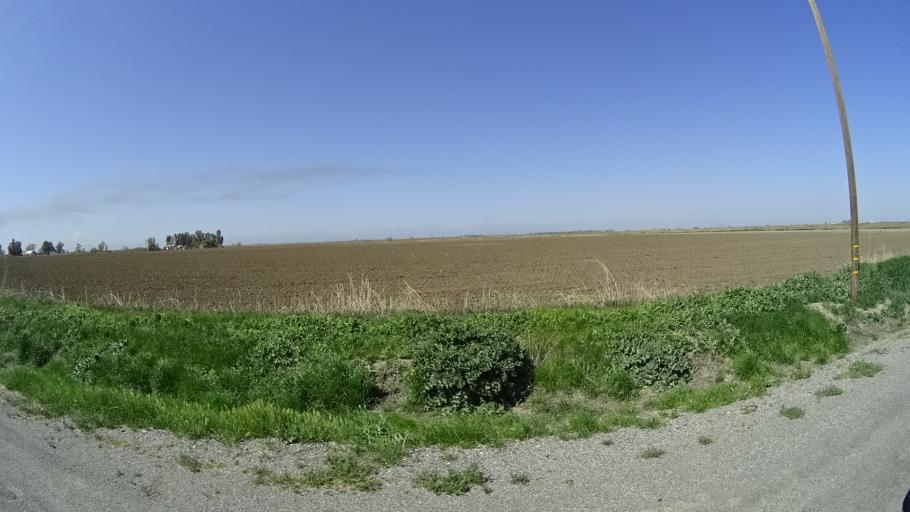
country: US
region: California
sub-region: Glenn County
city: Willows
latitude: 39.4282
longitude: -122.0457
